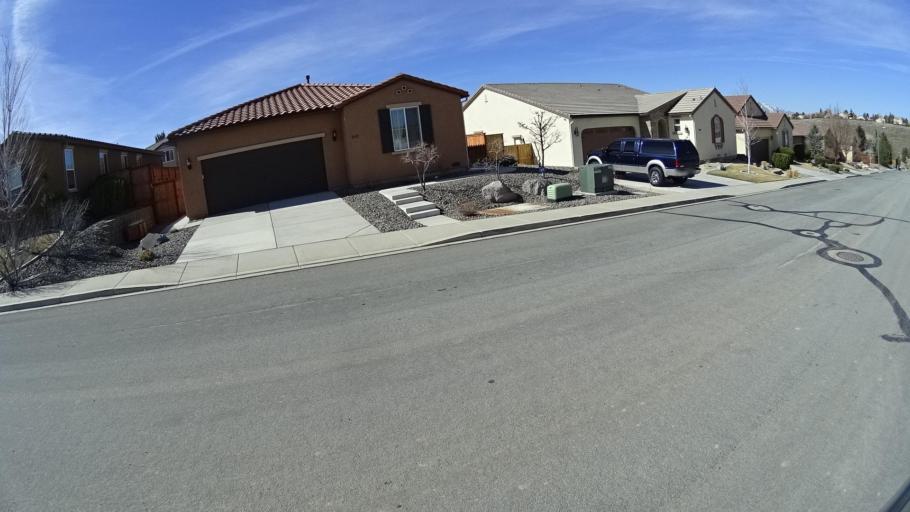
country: US
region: Nevada
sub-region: Washoe County
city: Spanish Springs
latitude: 39.5830
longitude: -119.6911
